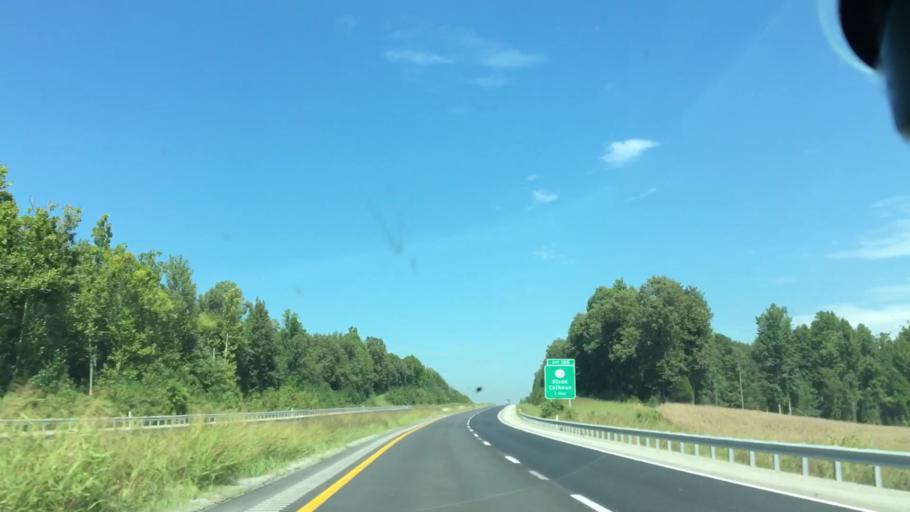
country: US
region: Kentucky
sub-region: Hopkins County
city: Madisonville
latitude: 37.4659
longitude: -87.4801
